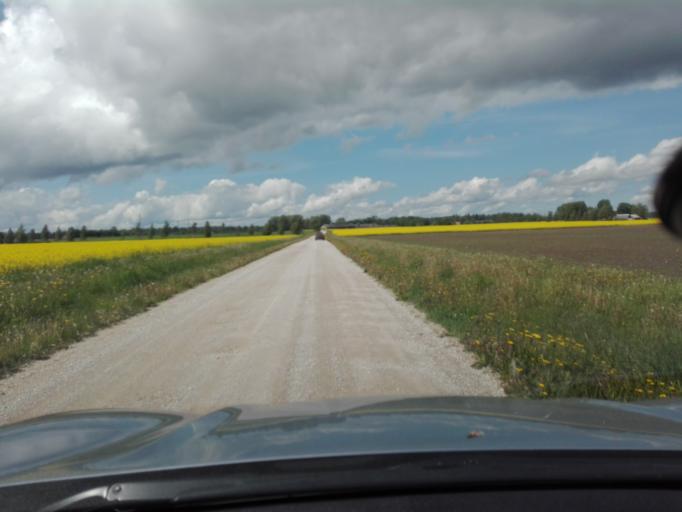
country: EE
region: Raplamaa
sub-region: Kehtna vald
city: Kehtna
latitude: 58.9646
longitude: 24.8870
